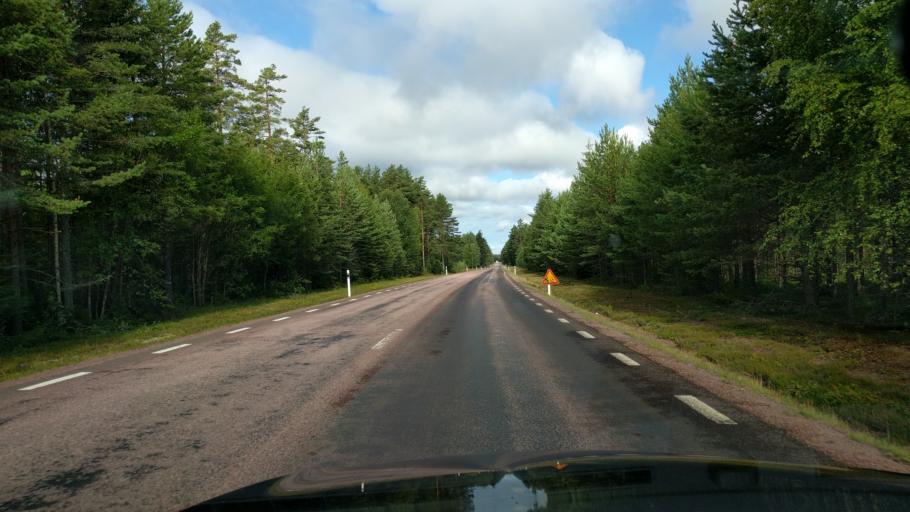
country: SE
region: Dalarna
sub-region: Mora Kommun
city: Mora
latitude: 61.0521
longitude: 14.4333
